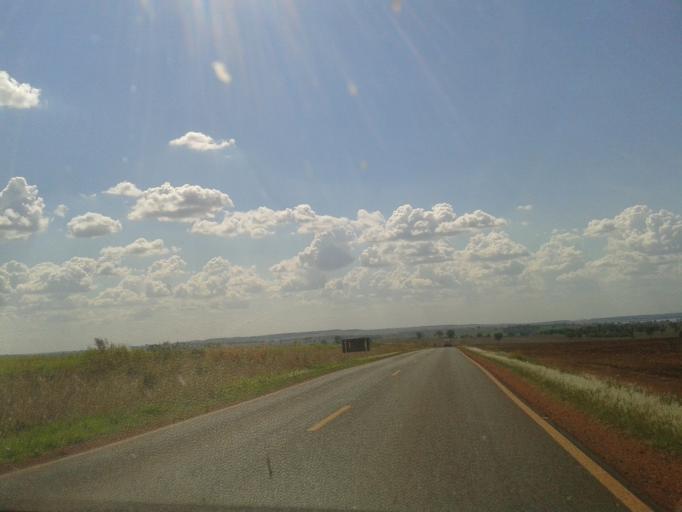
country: BR
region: Minas Gerais
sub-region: Centralina
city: Centralina
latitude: -18.6916
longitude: -49.3366
